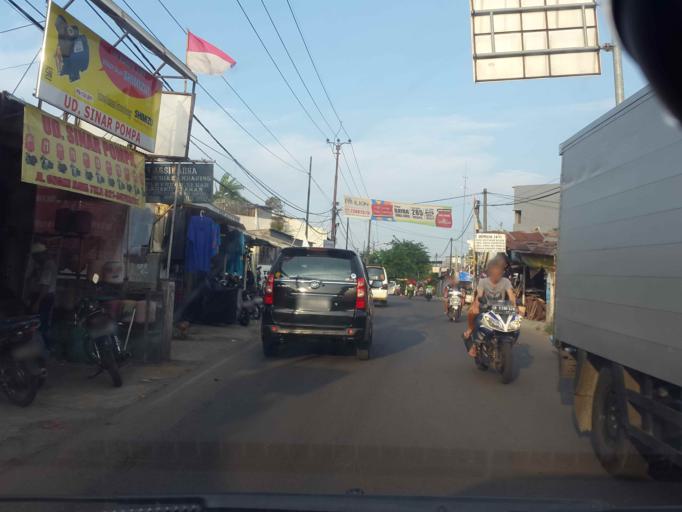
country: ID
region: Banten
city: South Tangerang
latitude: -6.2623
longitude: 106.7374
